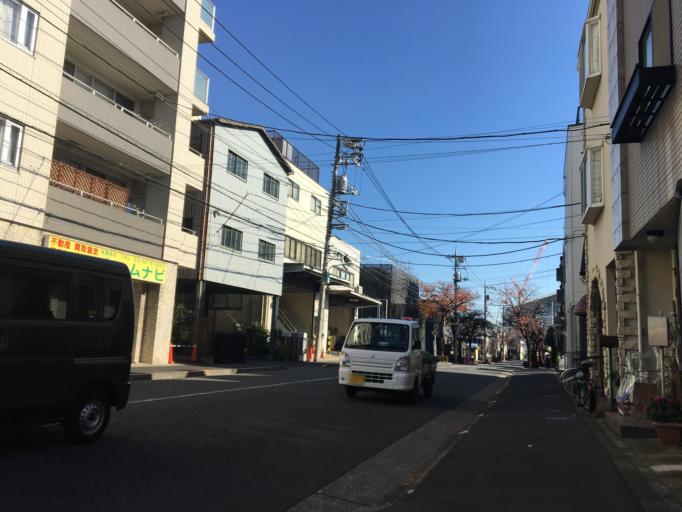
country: JP
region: Tokyo
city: Urayasu
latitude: 35.6878
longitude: 139.9002
